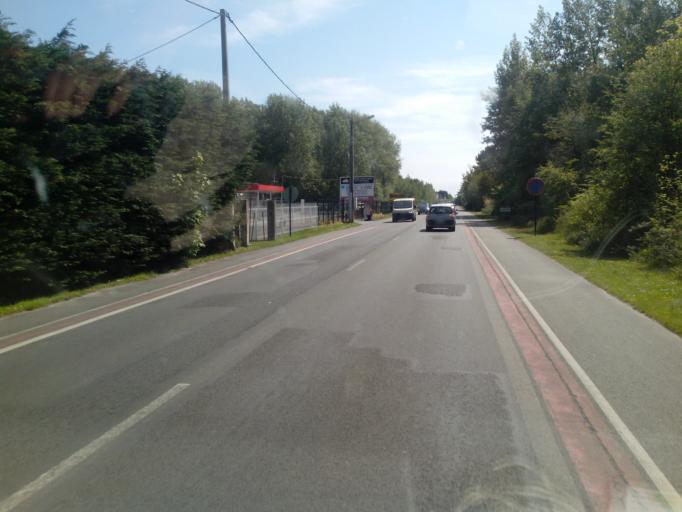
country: FR
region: Nord-Pas-de-Calais
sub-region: Departement du Pas-de-Calais
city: Merlimont
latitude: 50.4354
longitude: 1.6095
